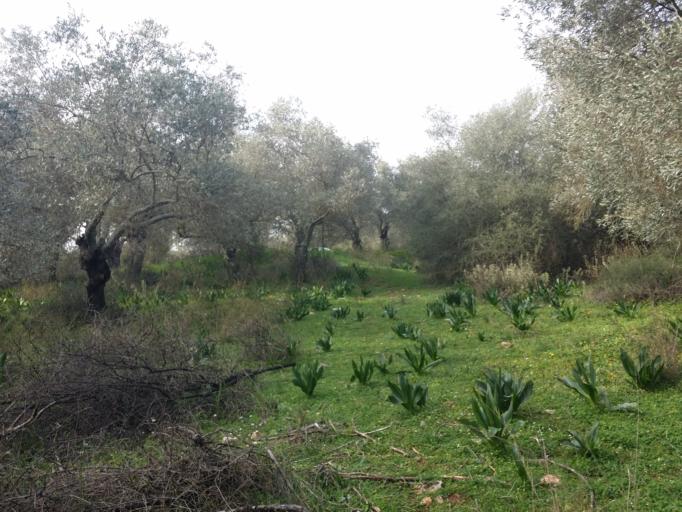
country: GR
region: West Greece
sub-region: Nomos Aitolias kai Akarnanias
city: Stanos
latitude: 38.7692
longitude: 21.1681
